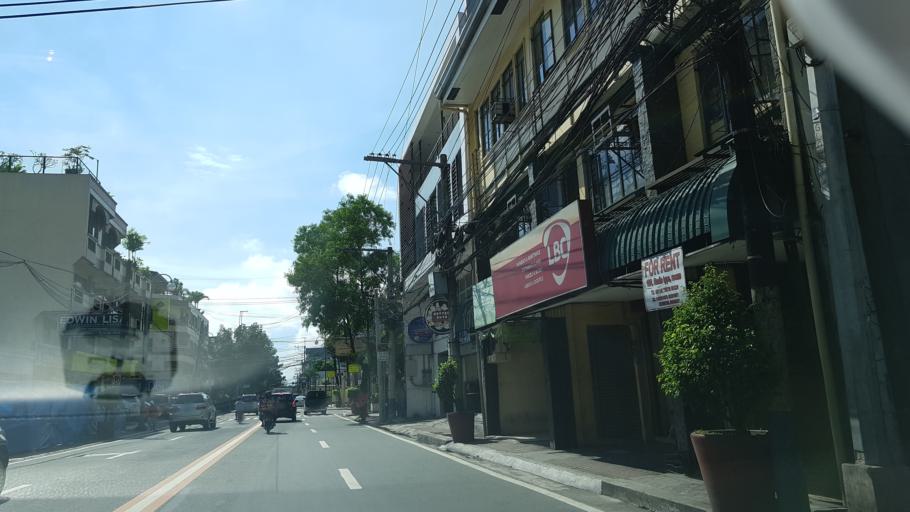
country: PH
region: Metro Manila
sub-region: Makati City
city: Makati City
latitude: 14.5688
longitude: 121.0273
